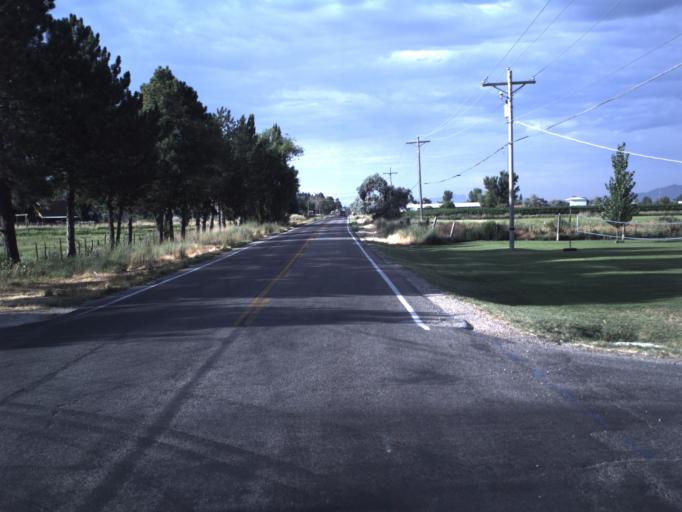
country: US
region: Utah
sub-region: Weber County
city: West Haven
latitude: 41.2201
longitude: -112.0929
